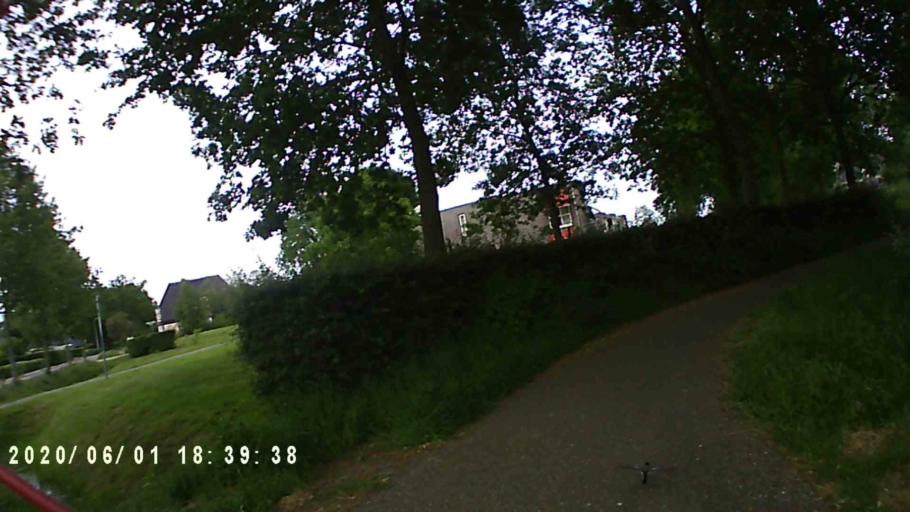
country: NL
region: Friesland
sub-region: Gemeente Tytsjerksteradiel
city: Eastermar
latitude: 53.1743
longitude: 6.0624
